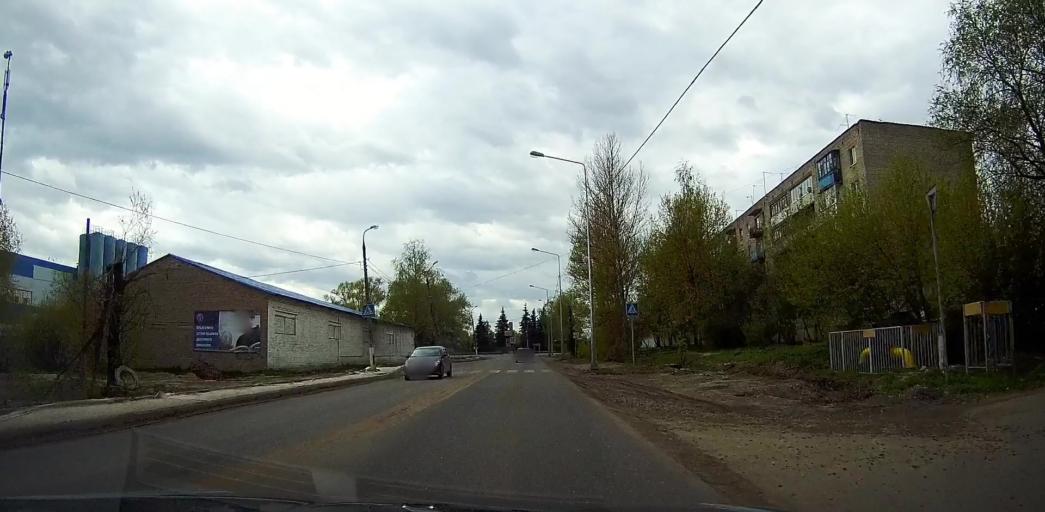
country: RU
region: Moskovskaya
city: Pavlovskiy Posad
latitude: 55.7745
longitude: 38.6863
